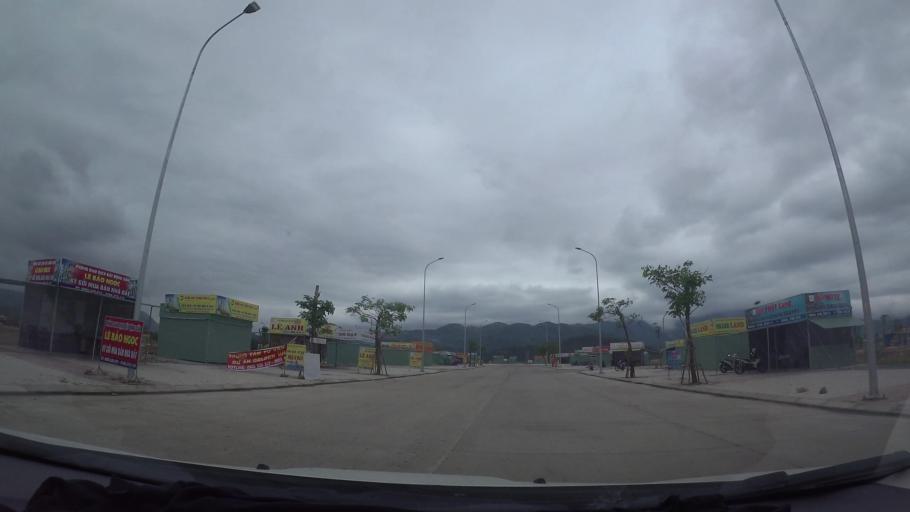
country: VN
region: Da Nang
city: Lien Chieu
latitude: 16.1065
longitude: 108.1165
